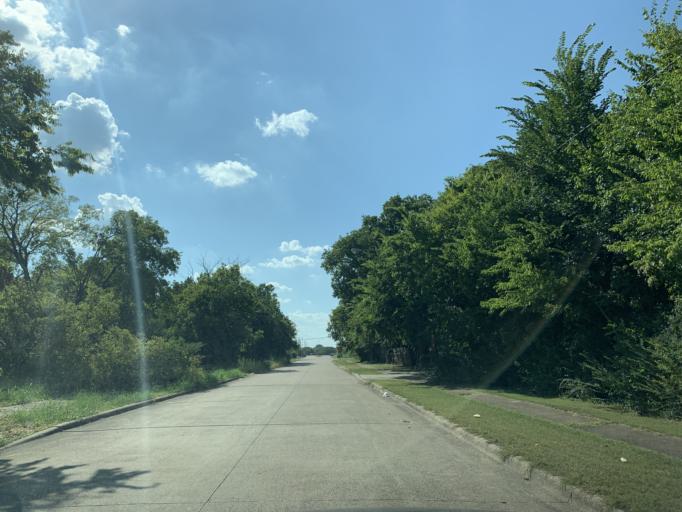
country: US
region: Texas
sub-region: Dallas County
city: Hutchins
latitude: 32.6545
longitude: -96.7704
